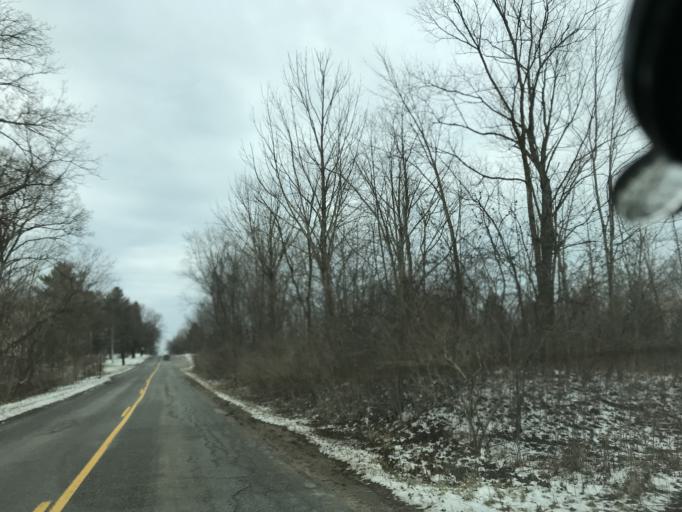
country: US
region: Michigan
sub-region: Kent County
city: East Grand Rapids
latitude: 42.9773
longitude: -85.5818
